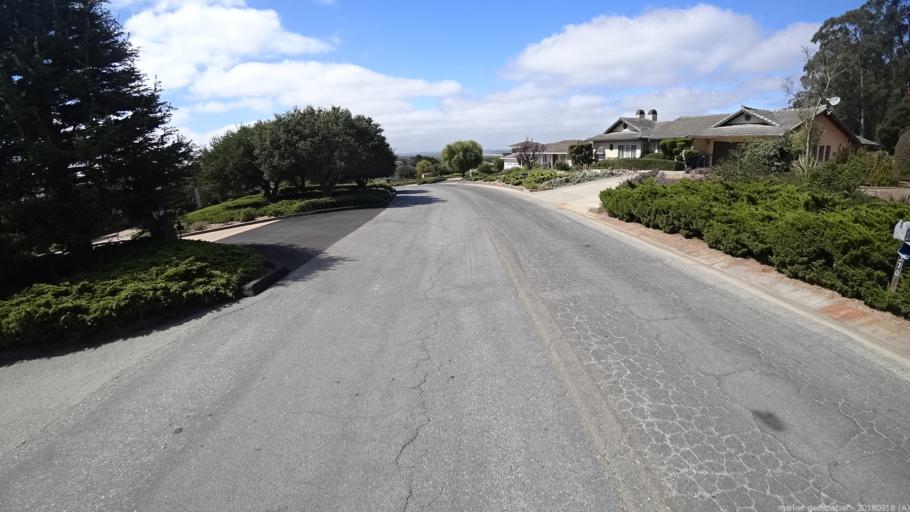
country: US
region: California
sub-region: Monterey County
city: Prunedale
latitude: 36.7650
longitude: -121.6598
